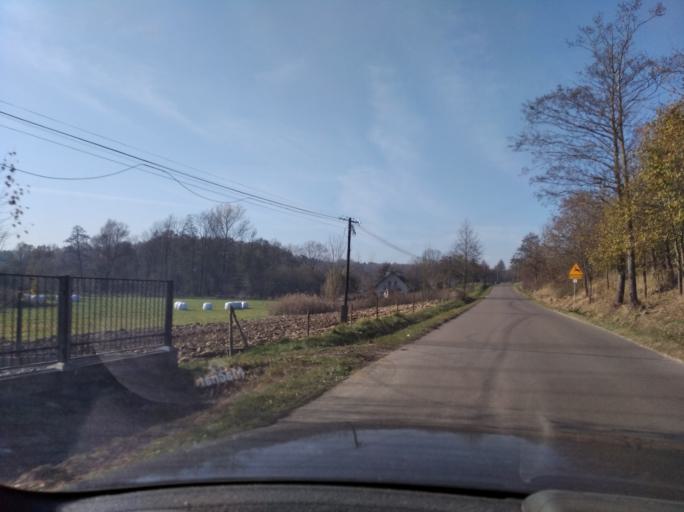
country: PL
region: Subcarpathian Voivodeship
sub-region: Powiat strzyzowski
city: Wisniowa
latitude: 49.8708
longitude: 21.6388
